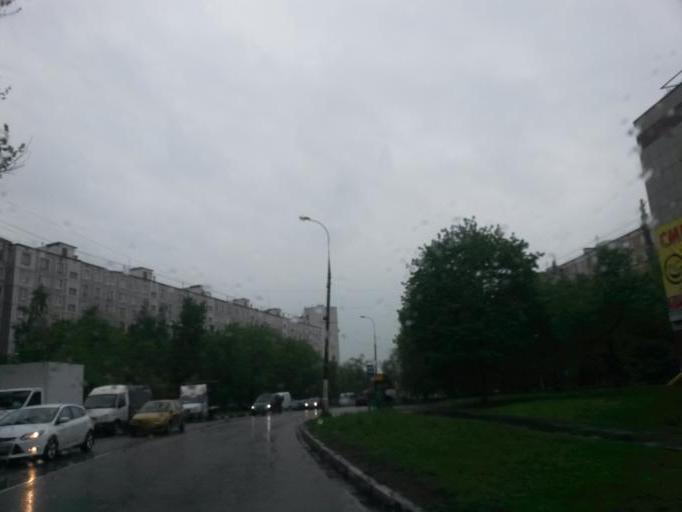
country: RU
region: Moscow
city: Zyablikovo
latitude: 55.6191
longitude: 37.7536
